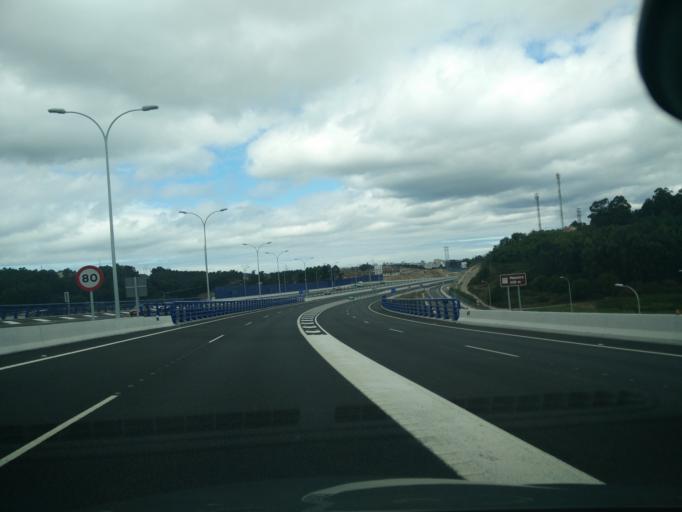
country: ES
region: Galicia
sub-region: Provincia da Coruna
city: A Coruna
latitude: 43.3285
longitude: -8.4232
